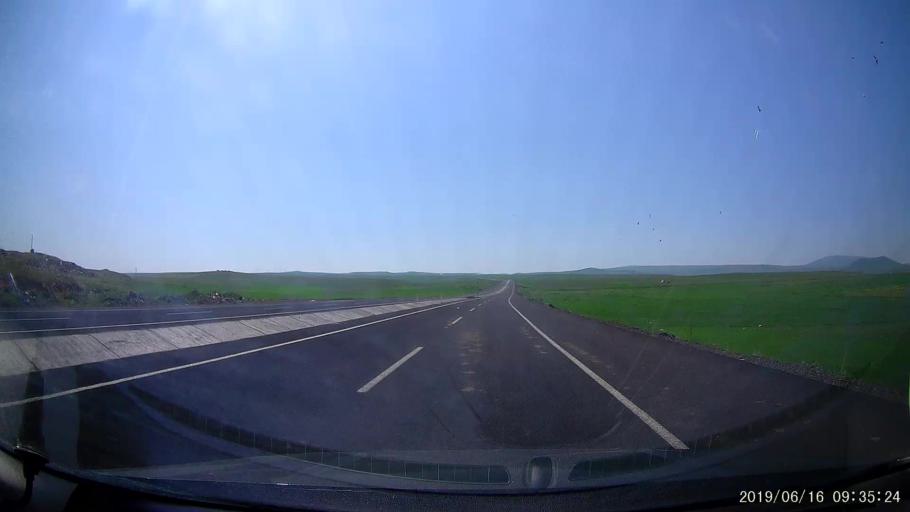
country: TR
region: Kars
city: Kars
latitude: 40.5727
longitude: 43.1552
